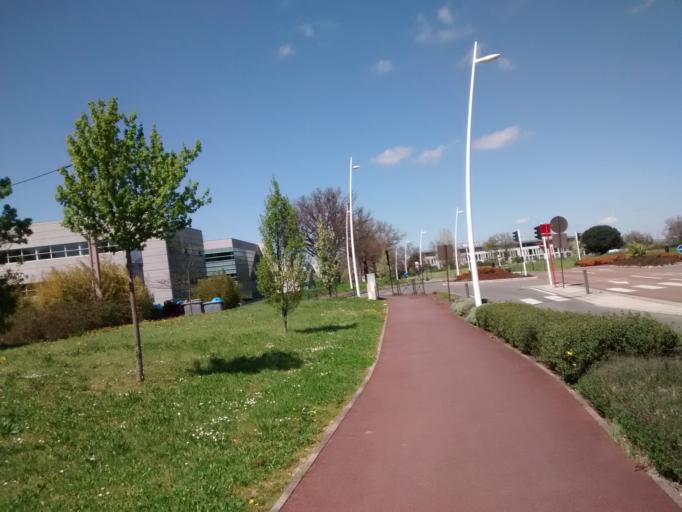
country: FR
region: Midi-Pyrenees
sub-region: Departement de la Haute-Garonne
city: Labege
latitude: 43.5345
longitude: 1.5208
